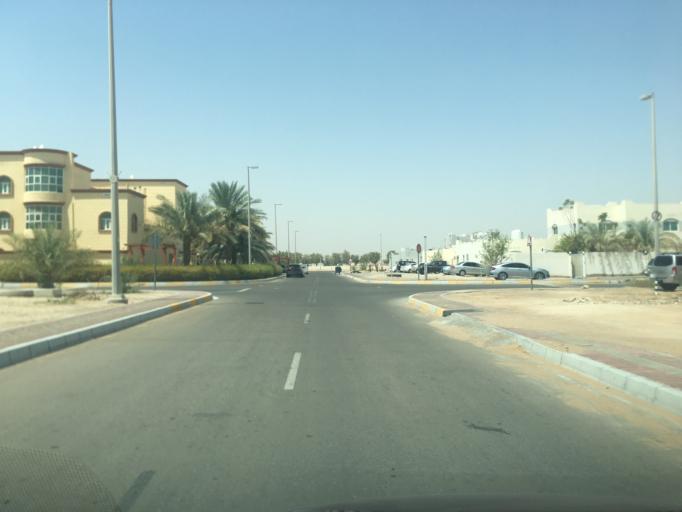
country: AE
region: Abu Dhabi
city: Abu Dhabi
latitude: 24.3089
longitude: 54.6357
